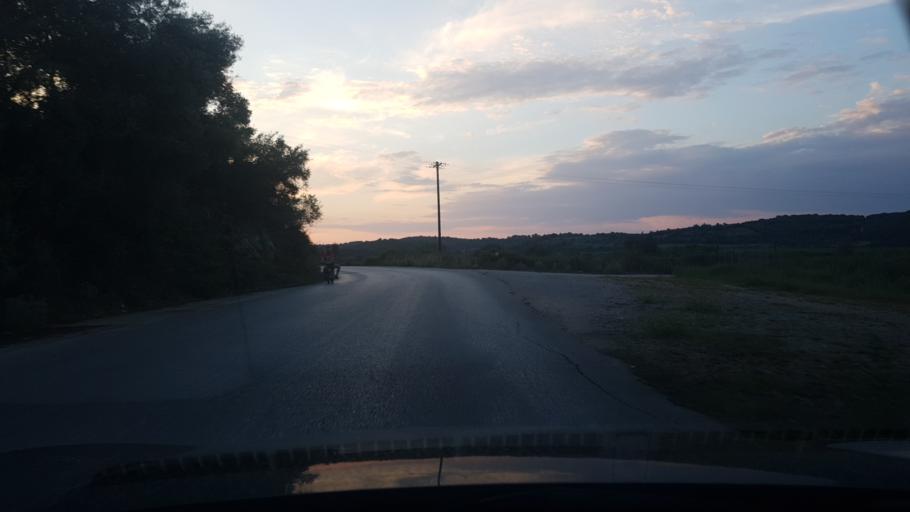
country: GR
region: West Greece
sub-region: Nomos Aitolias kai Akarnanias
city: Vonitsa
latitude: 38.9146
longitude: 20.8757
